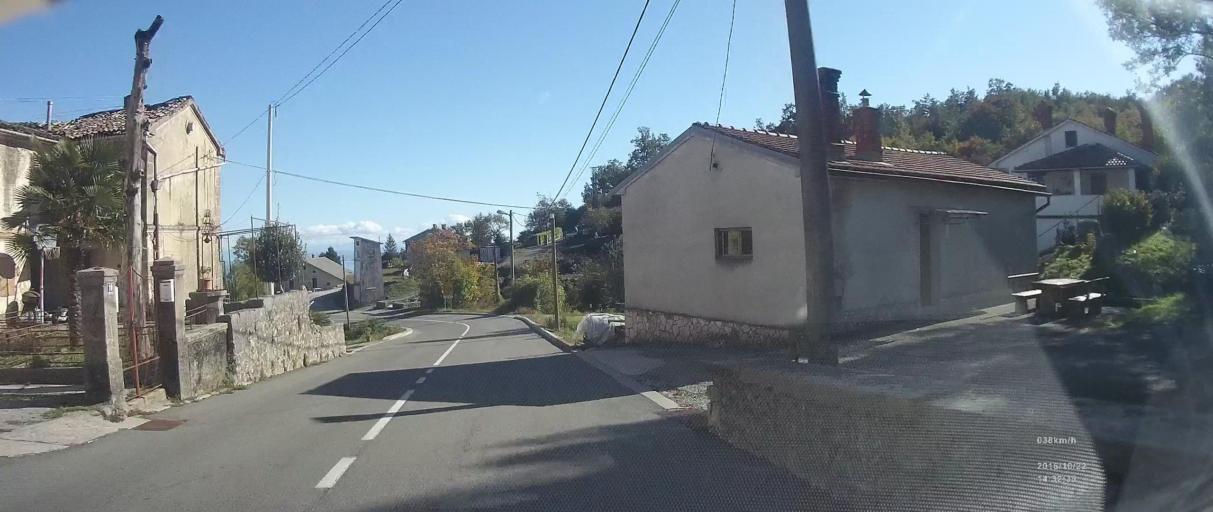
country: HR
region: Primorsko-Goranska
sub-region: Grad Opatija
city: Opatija
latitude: 45.3363
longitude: 14.2735
